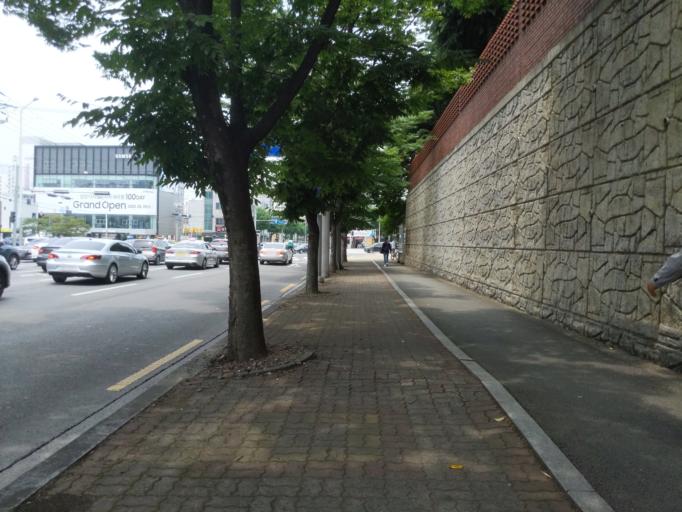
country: KR
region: Daegu
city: Hwawon
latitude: 35.8084
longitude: 128.5279
